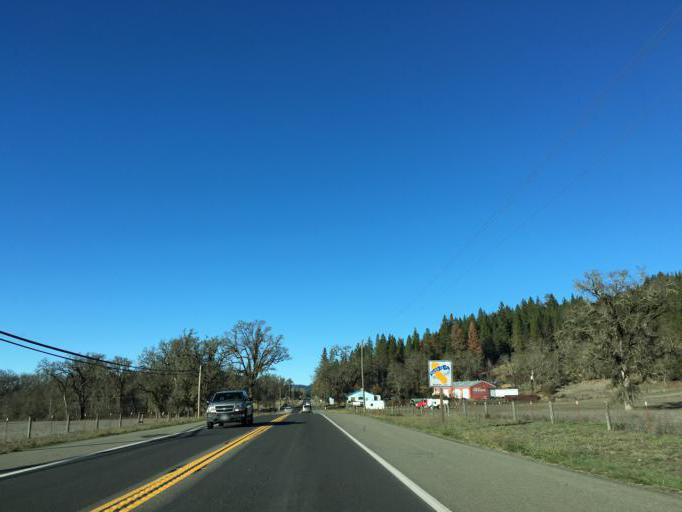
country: US
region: California
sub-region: Mendocino County
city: Laytonville
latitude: 39.6932
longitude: -123.4838
